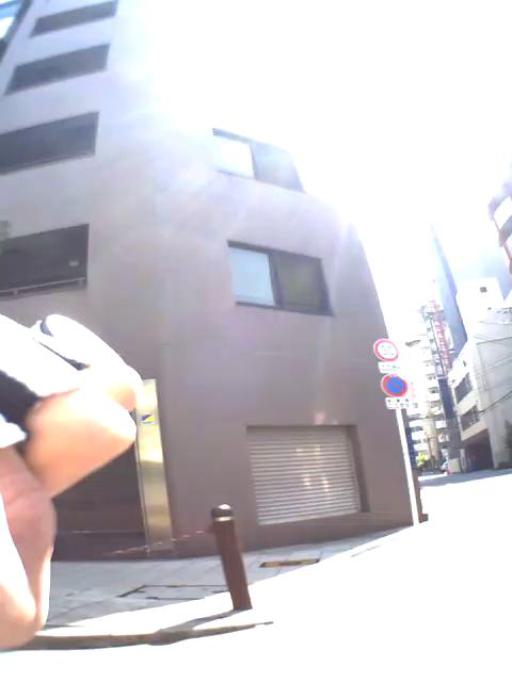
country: JP
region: Osaka
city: Osaka-shi
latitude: 34.6841
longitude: 135.5115
